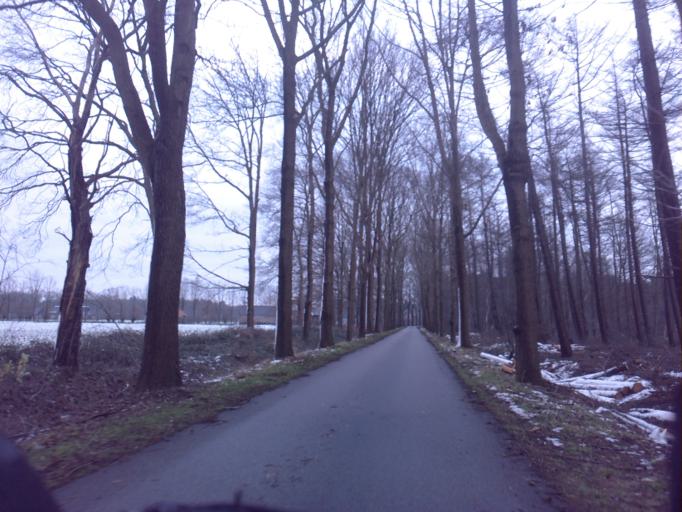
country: NL
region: Utrecht
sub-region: Gemeente Utrechtse Heuvelrug
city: Overberg
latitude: 52.1003
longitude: 5.4850
